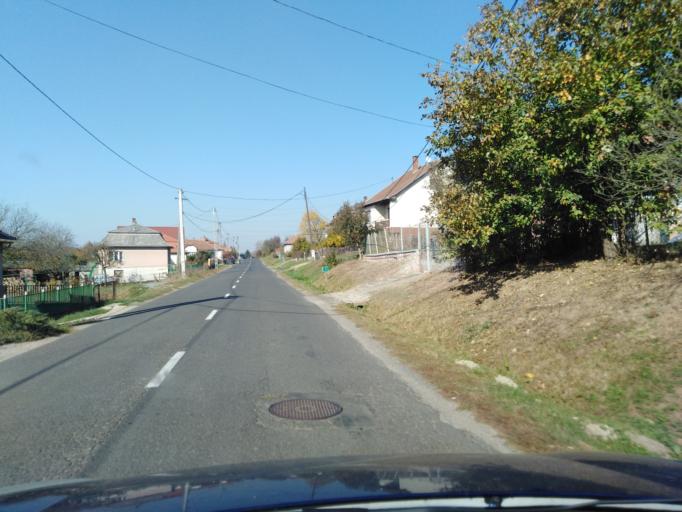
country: HU
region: Nograd
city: Karancskeszi
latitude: 48.1769
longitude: 19.6735
